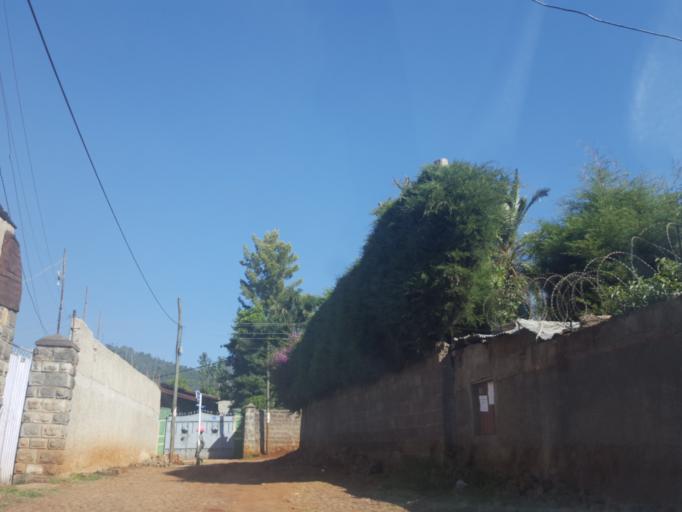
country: ET
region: Adis Abeba
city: Addis Ababa
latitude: 9.0557
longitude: 38.7481
